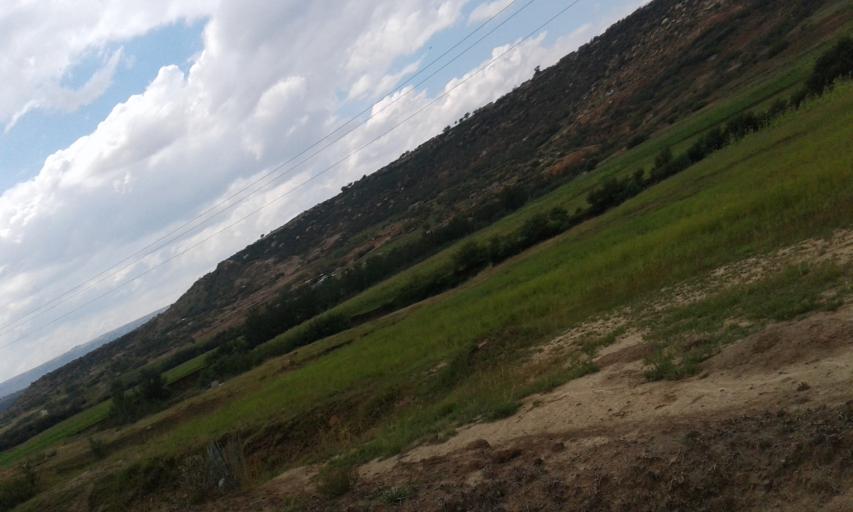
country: LS
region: Maseru
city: Maseru
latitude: -29.4164
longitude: 27.5711
